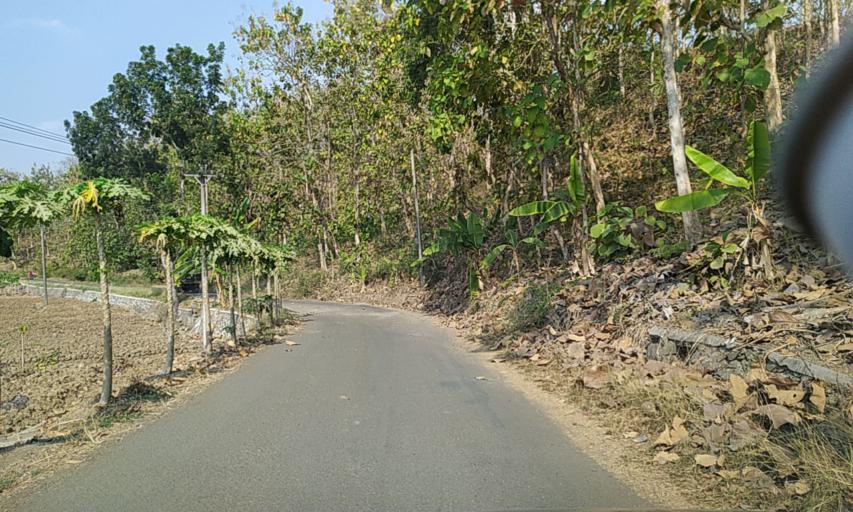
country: ID
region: Central Java
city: Muktisari
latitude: -7.5048
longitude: 108.8823
